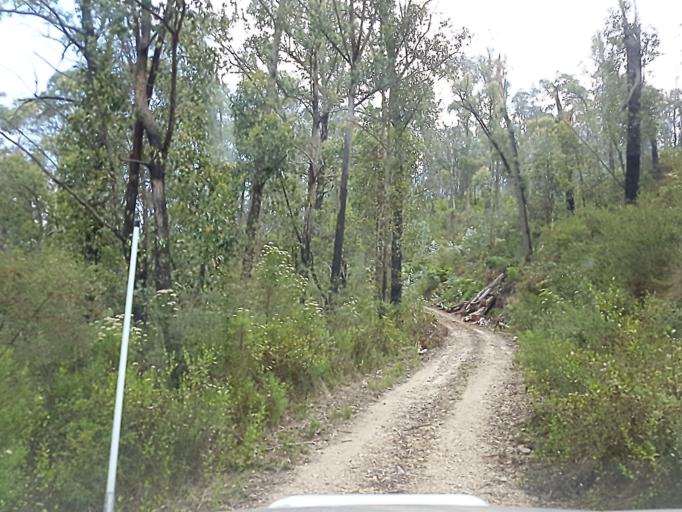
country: AU
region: Victoria
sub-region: East Gippsland
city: Lakes Entrance
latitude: -37.3463
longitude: 148.3470
